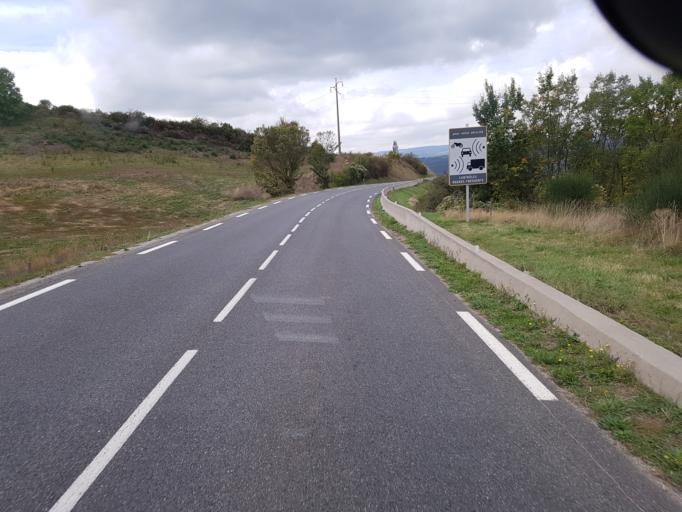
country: FR
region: Midi-Pyrenees
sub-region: Departement de l'Aveyron
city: Saint-Georges-de-Luzencon
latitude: 44.0782
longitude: 3.0113
